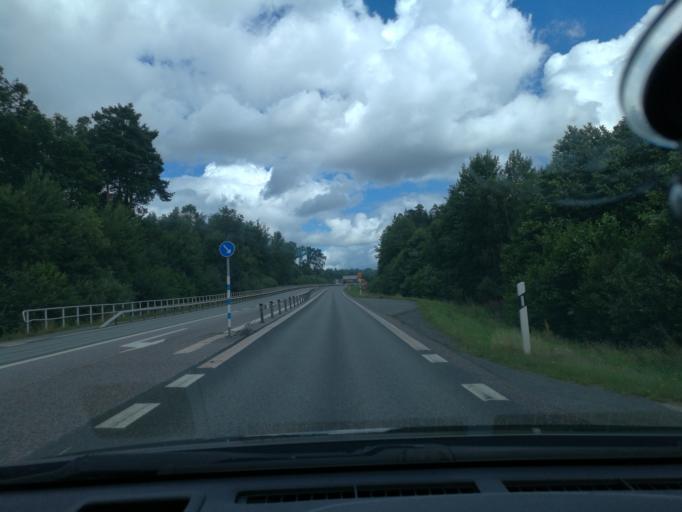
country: SE
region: Skane
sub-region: Hassleholms Kommun
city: Hastveda
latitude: 56.2247
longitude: 13.8842
